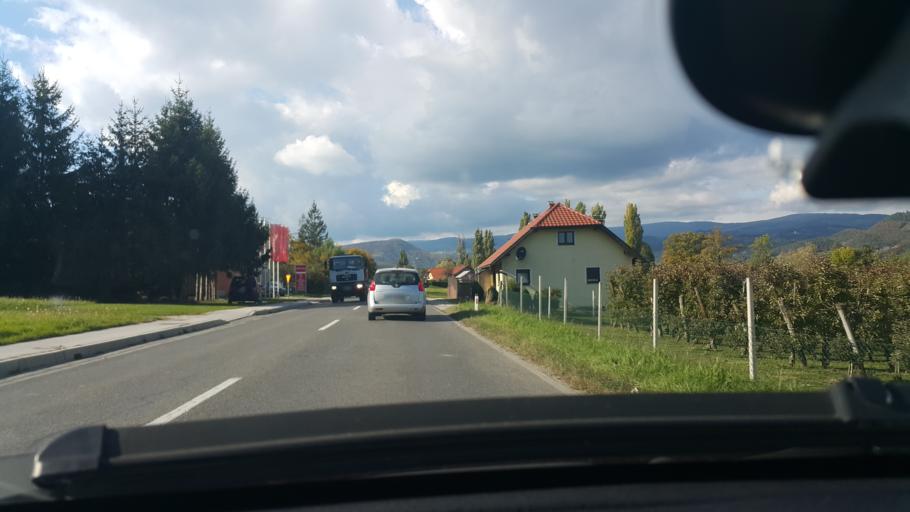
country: SI
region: Slovenska Konjice
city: Slovenske Konjice
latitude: 46.3437
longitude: 15.4120
